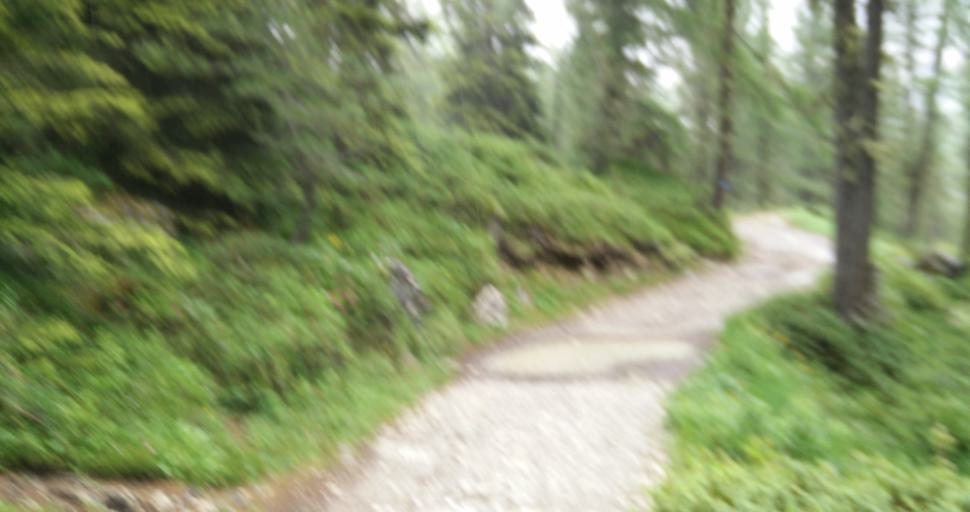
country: IT
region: Trentino-Alto Adige
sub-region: Provincia di Trento
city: Vigo di Fassa
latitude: 46.4360
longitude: 11.6523
